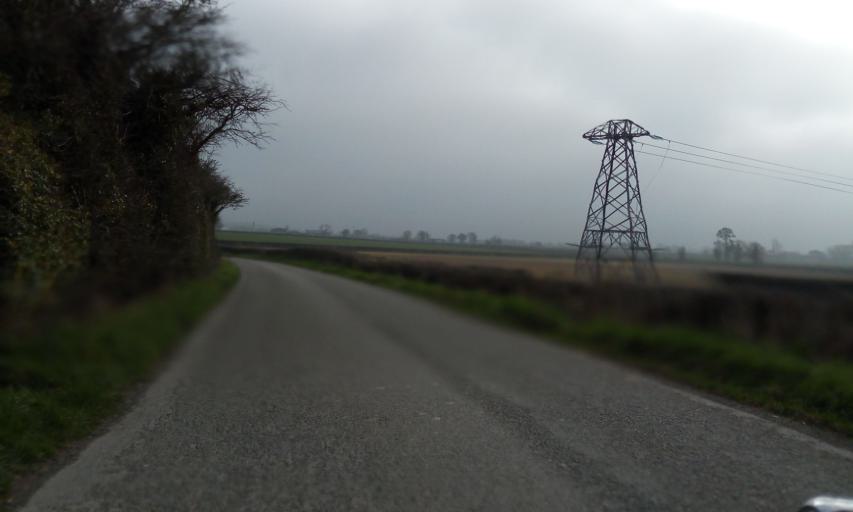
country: IE
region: Leinster
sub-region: Kilkenny
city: Kilkenny
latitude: 52.6582
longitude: -7.1758
